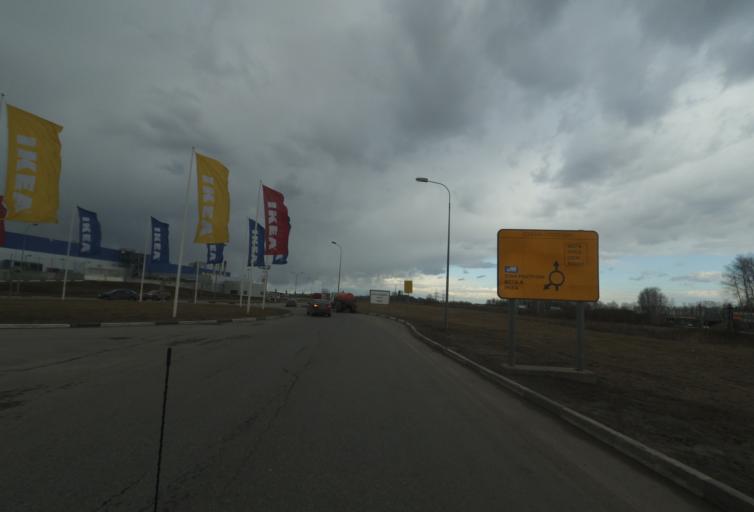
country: RU
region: Nizjnij Novgorod
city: Afonino
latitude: 56.2219
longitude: 44.0715
